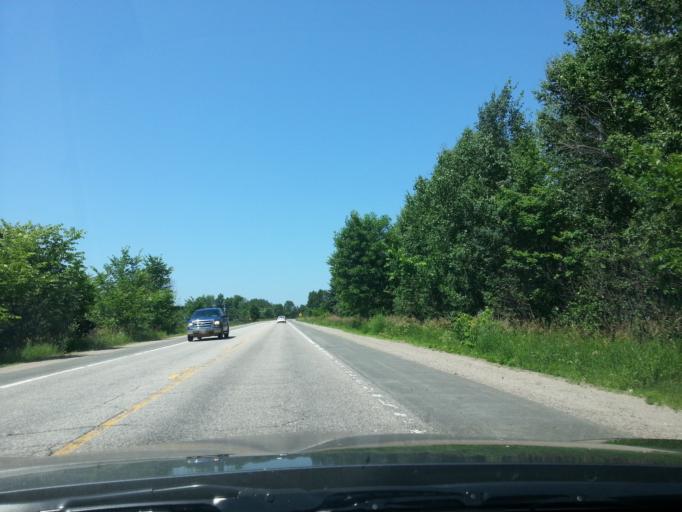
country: CA
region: Ontario
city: Arnprior
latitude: 45.5542
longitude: -76.1165
